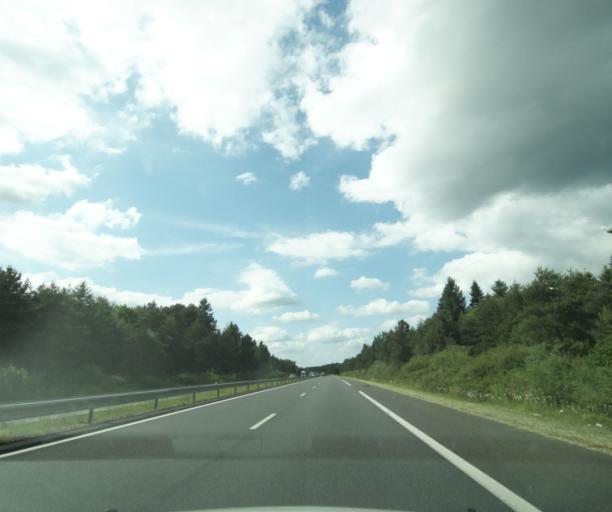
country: FR
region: Centre
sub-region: Departement du Loir-et-Cher
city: Chaumont-sur-Tharonne
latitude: 47.6289
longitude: 1.9573
